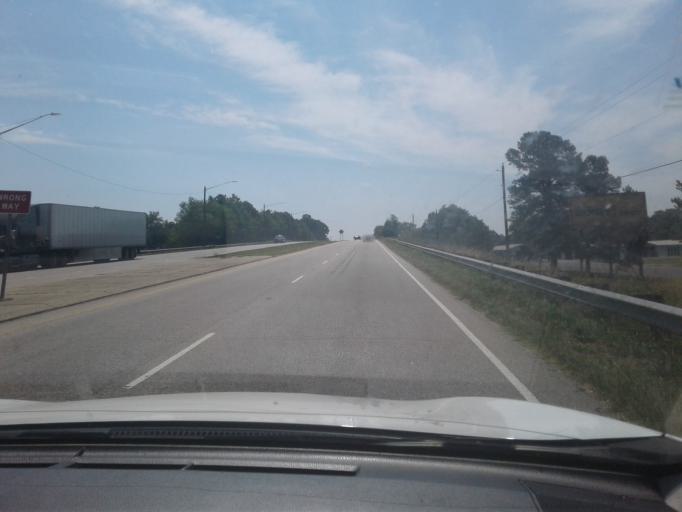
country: US
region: North Carolina
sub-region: Harnett County
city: Erwin
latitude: 35.3308
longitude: -78.6657
